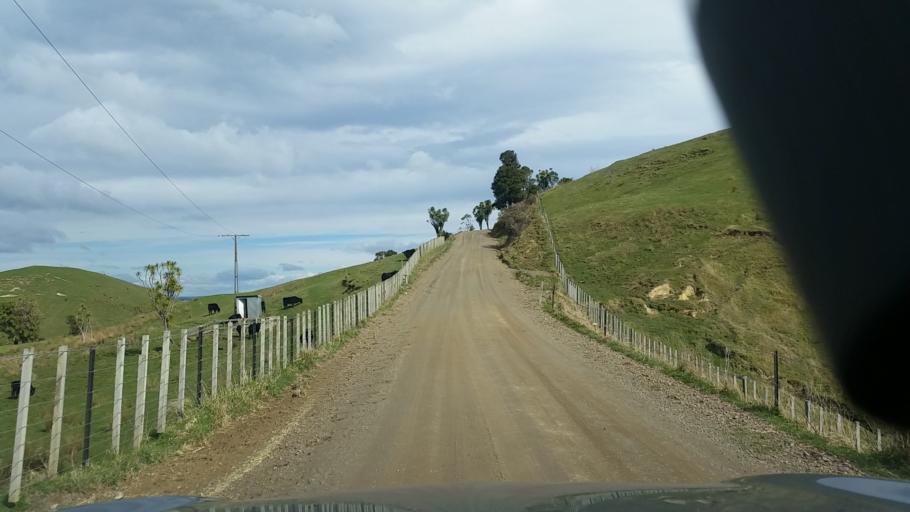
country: NZ
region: Hawke's Bay
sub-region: Napier City
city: Napier
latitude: -39.2098
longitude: 176.9628
